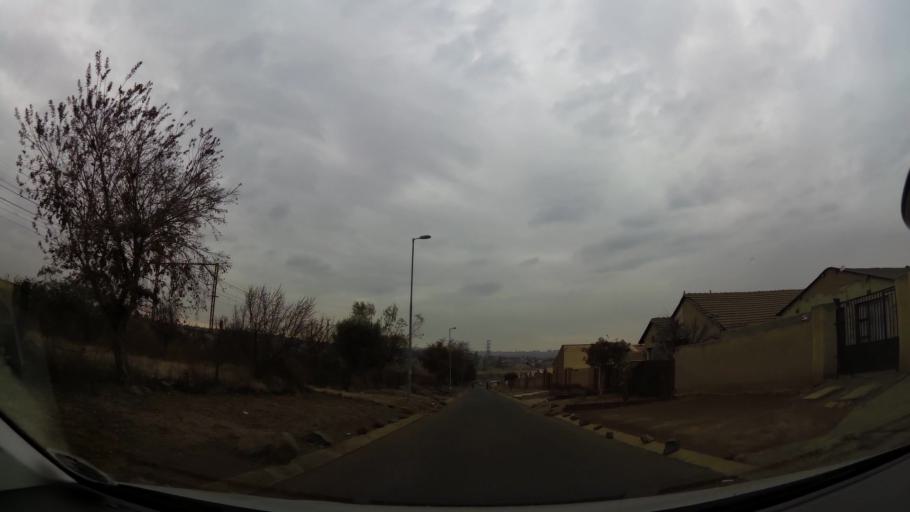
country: ZA
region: Gauteng
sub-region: City of Johannesburg Metropolitan Municipality
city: Soweto
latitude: -26.2422
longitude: 27.8692
